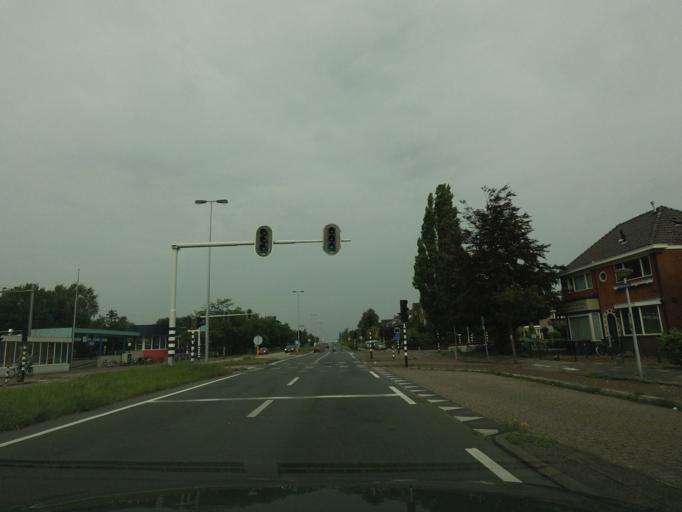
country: NL
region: North Holland
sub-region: Gemeente Zaanstad
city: Zaanstad
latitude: 52.4572
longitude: 4.8063
